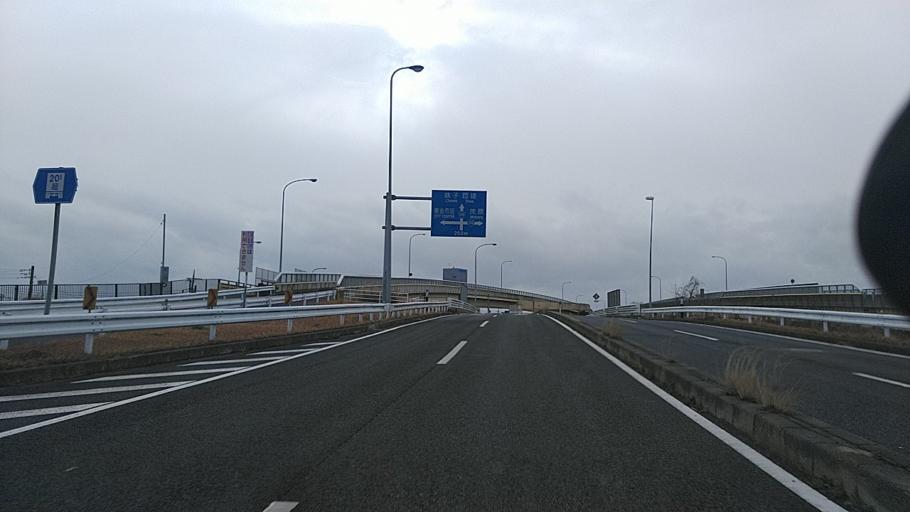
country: JP
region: Chiba
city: Togane
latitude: 35.5527
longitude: 140.3482
